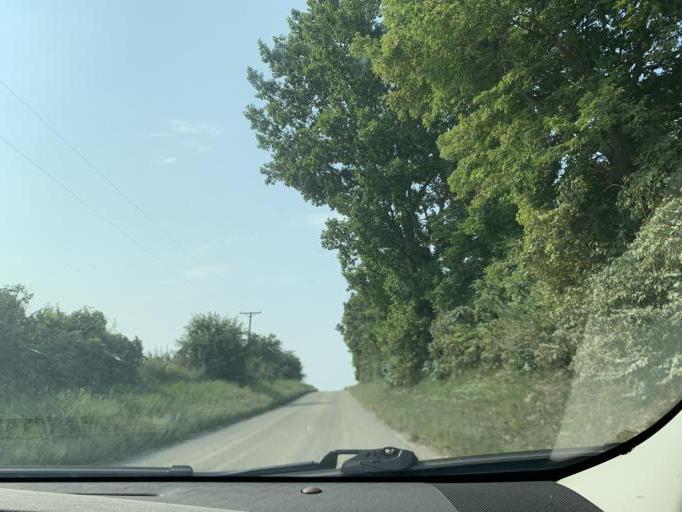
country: US
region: Illinois
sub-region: Whiteside County
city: Sterling
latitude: 41.8312
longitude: -89.7471
